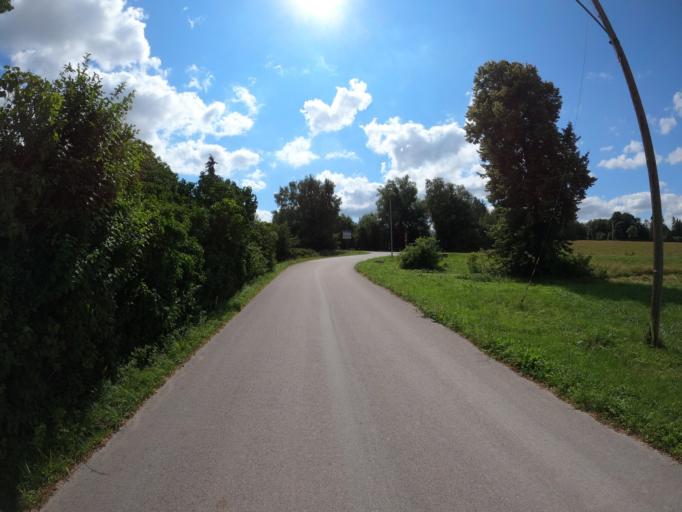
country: SE
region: Skane
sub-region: Lunds Kommun
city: Veberod
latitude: 55.5900
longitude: 13.4965
